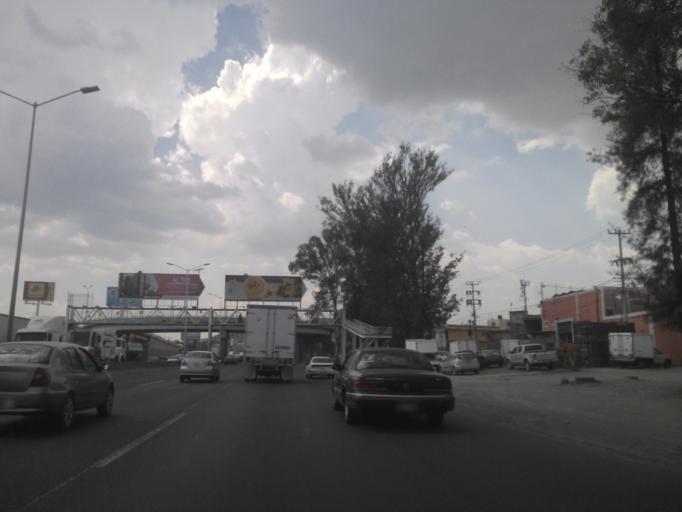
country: MX
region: Jalisco
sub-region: San Pedro Tlaquepaque
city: Paseo del Prado
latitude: 20.6001
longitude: -103.3941
